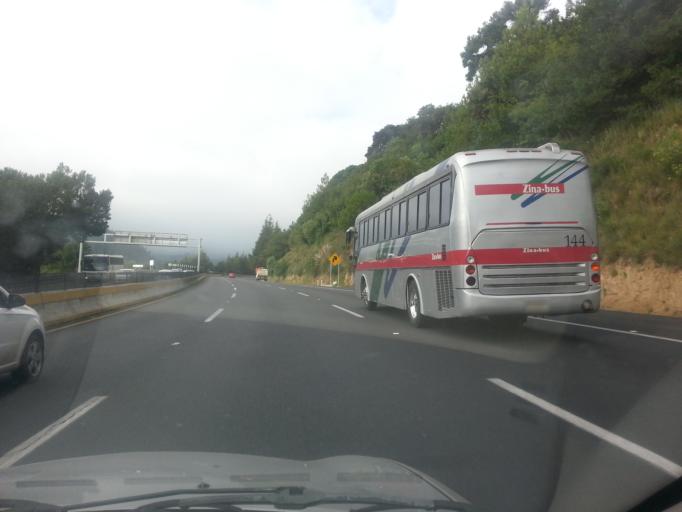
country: MX
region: Mexico City
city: Cuajimalpa
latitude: 19.3395
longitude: -99.2972
